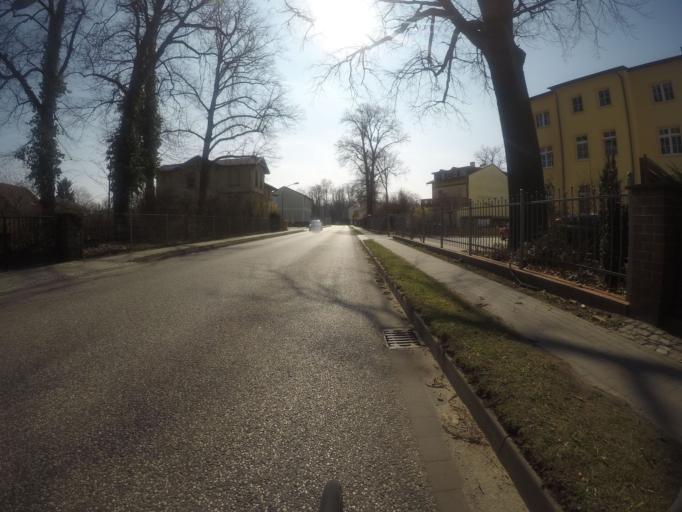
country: DE
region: Brandenburg
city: Konigs Wusterhausen
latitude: 52.2992
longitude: 13.6505
